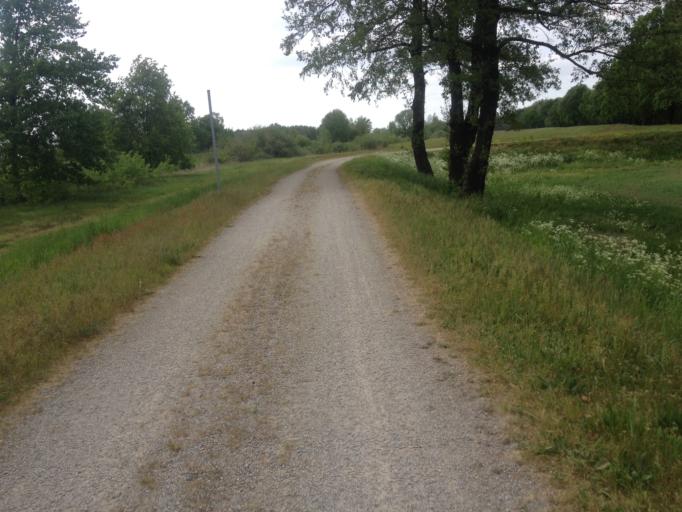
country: DE
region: Brandenburg
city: Drehnow
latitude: 51.8275
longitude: 14.3509
